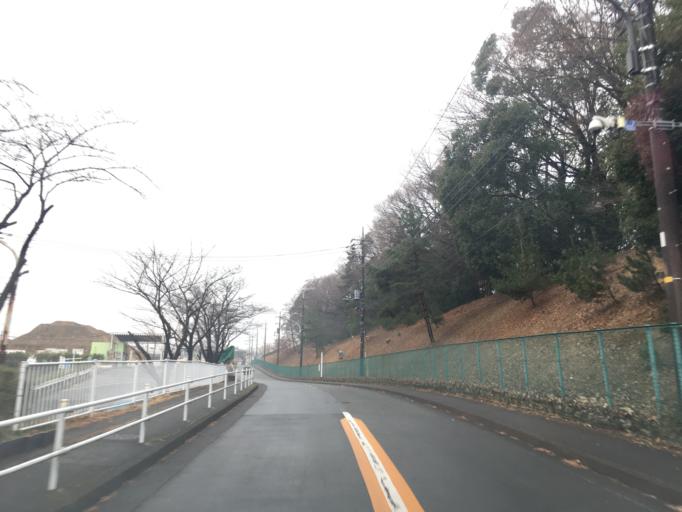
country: JP
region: Tokyo
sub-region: Machida-shi
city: Machida
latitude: 35.5881
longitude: 139.4104
